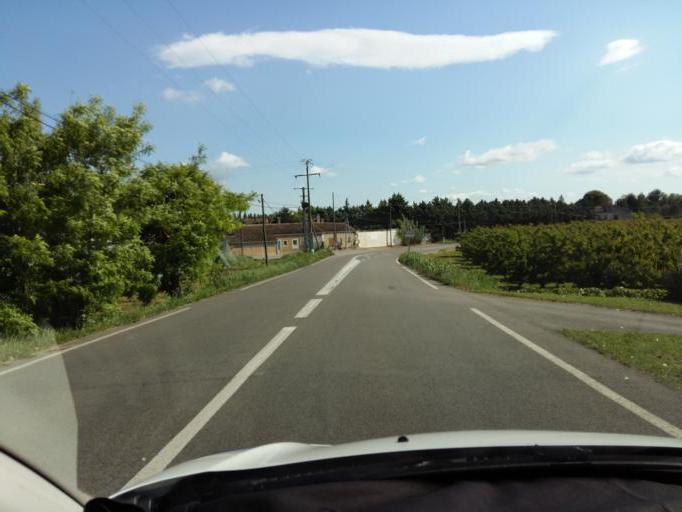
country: FR
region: Provence-Alpes-Cote d'Azur
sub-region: Departement du Vaucluse
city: Cavaillon
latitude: 43.8487
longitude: 5.0604
